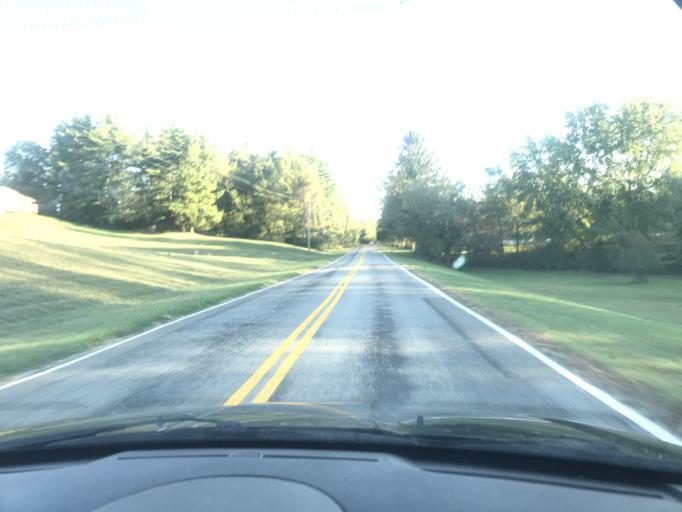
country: US
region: Ohio
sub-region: Logan County
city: De Graff
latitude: 40.2466
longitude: -83.8654
